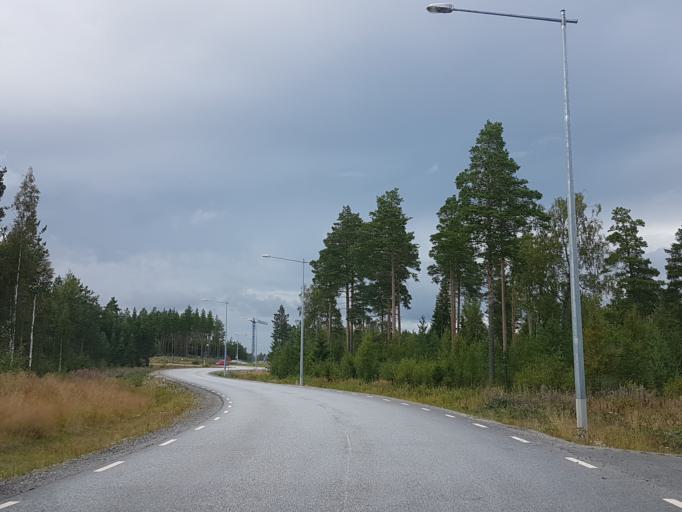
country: SE
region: Vaesterbotten
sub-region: Umea Kommun
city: Ersmark
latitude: 63.8014
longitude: 20.3647
